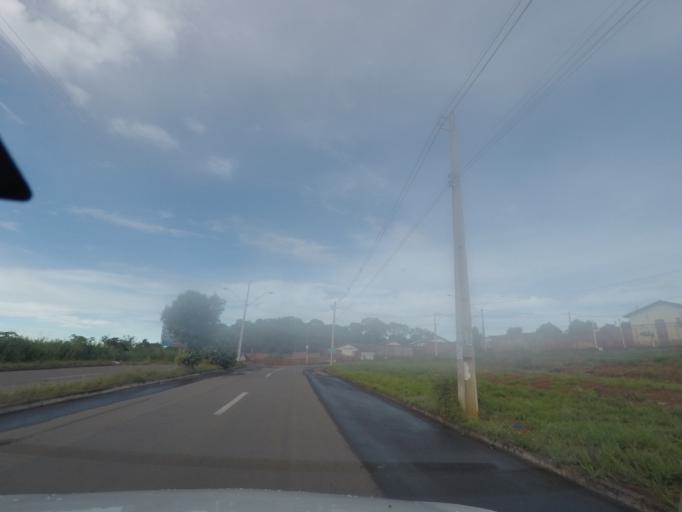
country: BR
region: Goias
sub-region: Aparecida De Goiania
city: Aparecida de Goiania
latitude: -16.7851
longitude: -49.3797
